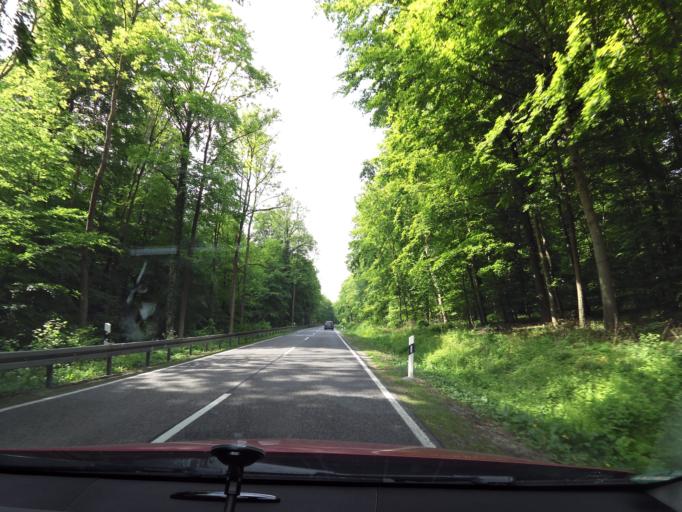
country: DE
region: Thuringia
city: Hallungen
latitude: 51.1356
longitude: 10.3705
